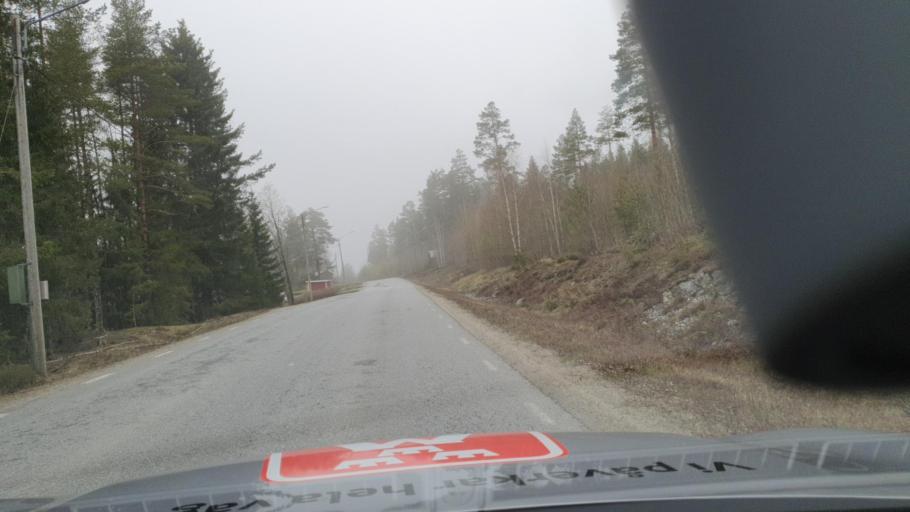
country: SE
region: Vaesternorrland
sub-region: OErnskoeldsviks Kommun
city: Husum
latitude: 63.4859
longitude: 19.1850
